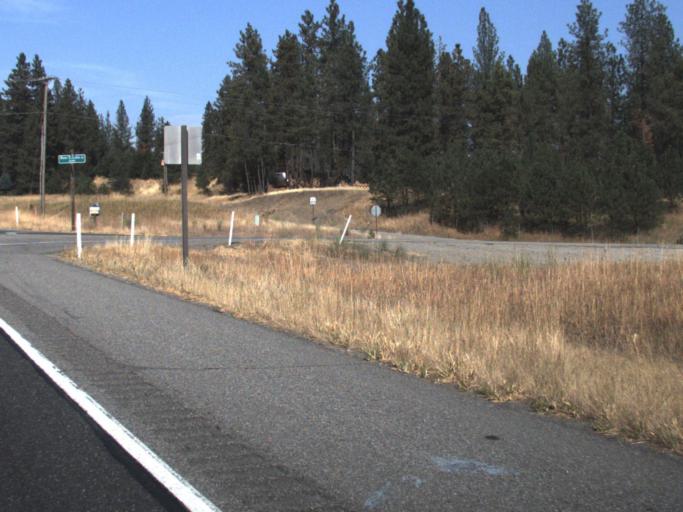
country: US
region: Washington
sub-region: Spokane County
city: Mead
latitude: 47.8957
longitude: -117.3524
